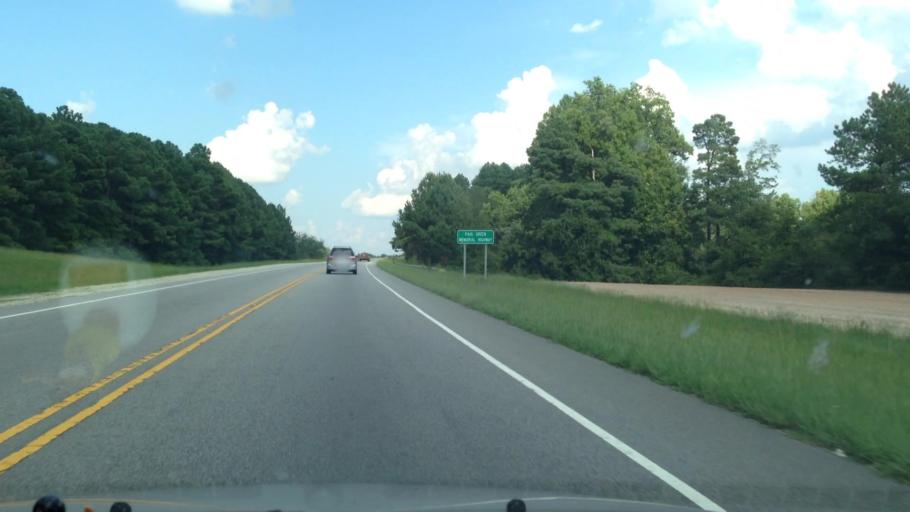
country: US
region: North Carolina
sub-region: Lee County
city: Broadway
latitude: 35.4390
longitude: -79.0470
